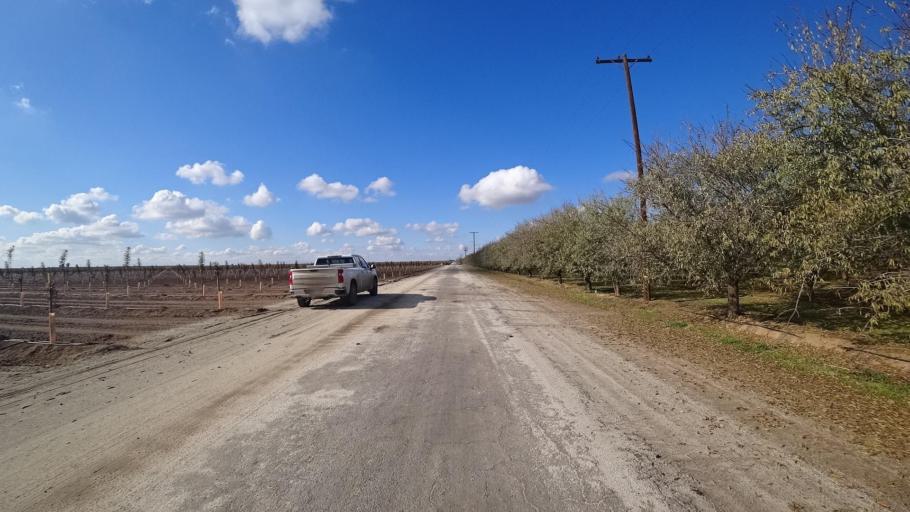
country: US
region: California
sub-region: Kern County
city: McFarland
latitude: 35.6600
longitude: -119.2066
